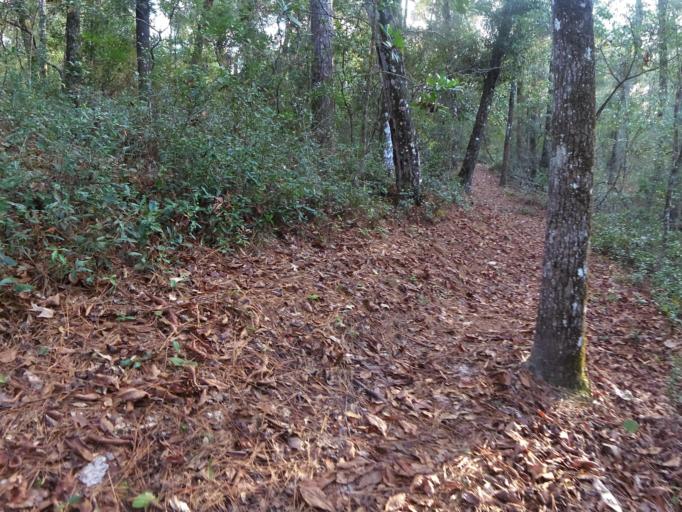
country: US
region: Florida
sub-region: Clay County
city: Middleburg
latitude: 30.1417
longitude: -81.9326
